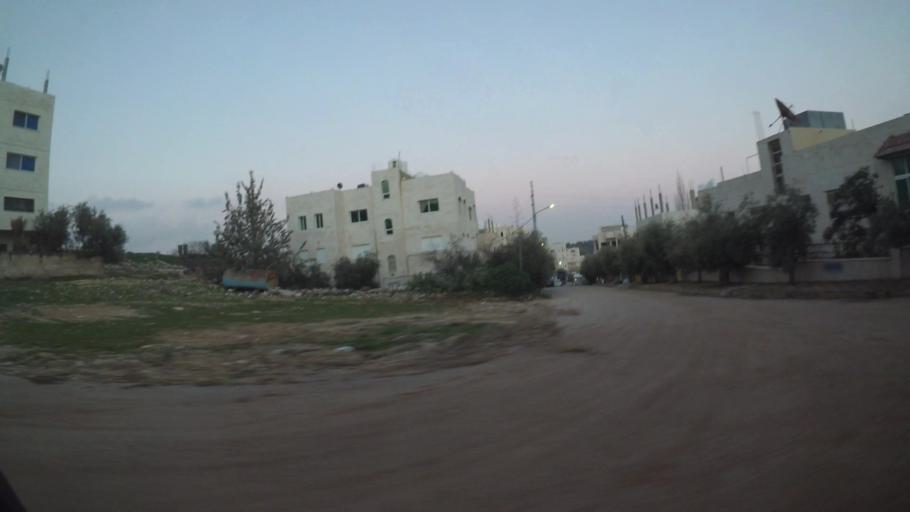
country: JO
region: Amman
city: Al Bunayyat ash Shamaliyah
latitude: 31.8897
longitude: 35.9208
